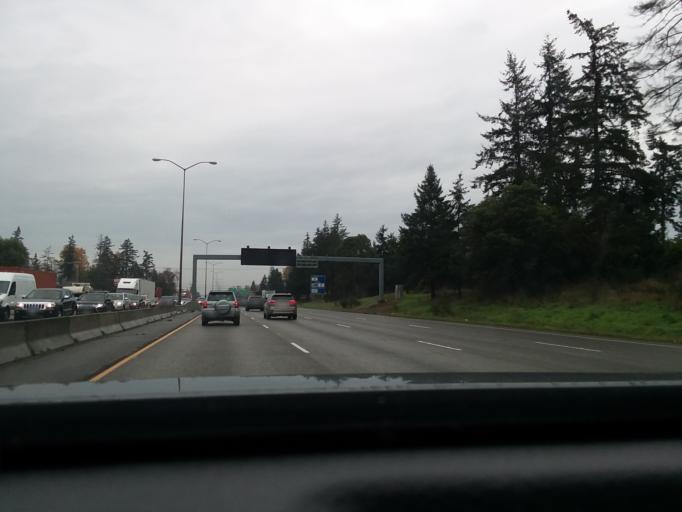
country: US
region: Washington
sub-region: Pierce County
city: McChord Air Force Base
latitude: 47.1428
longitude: -122.5125
